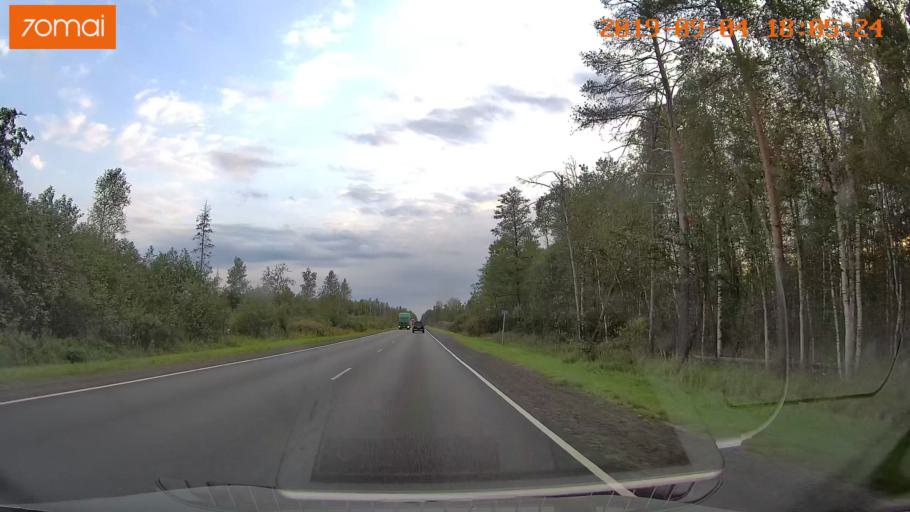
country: RU
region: Moskovskaya
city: Il'inskiy Pogost
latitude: 55.4418
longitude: 38.8271
